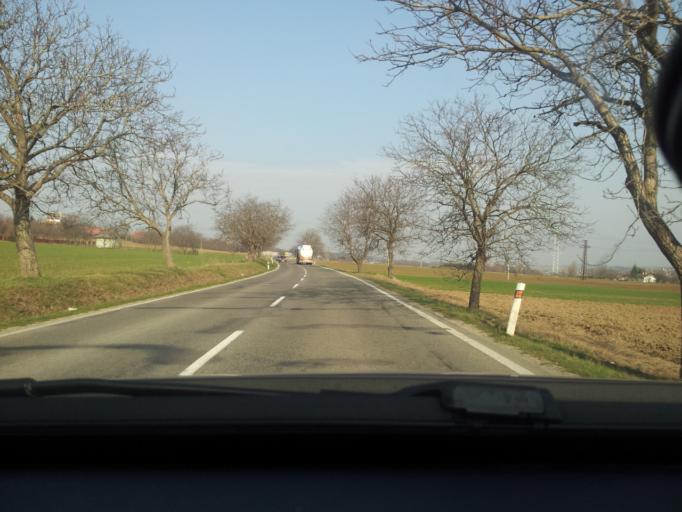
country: SK
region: Trnavsky
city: Hlohovec
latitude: 48.3736
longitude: 17.8852
